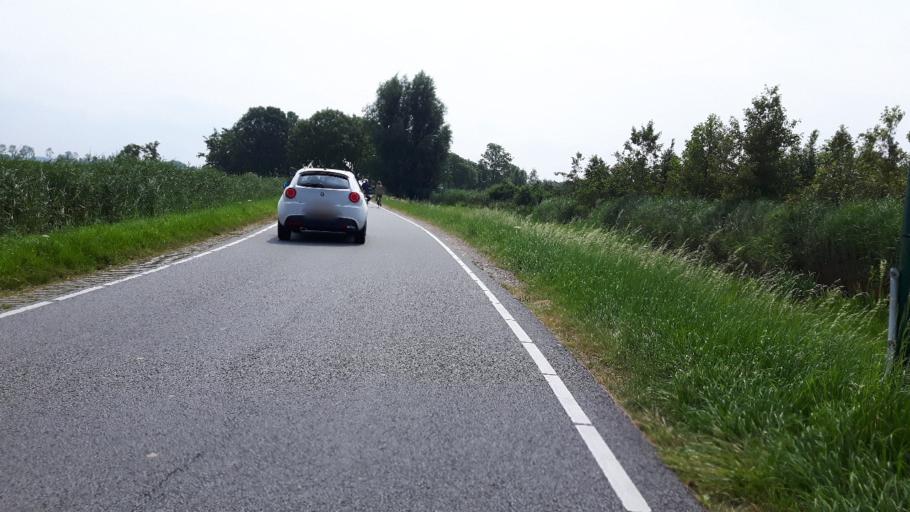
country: NL
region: Utrecht
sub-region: Gemeente IJsselstein
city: IJsselstein
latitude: 52.0549
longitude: 5.0144
